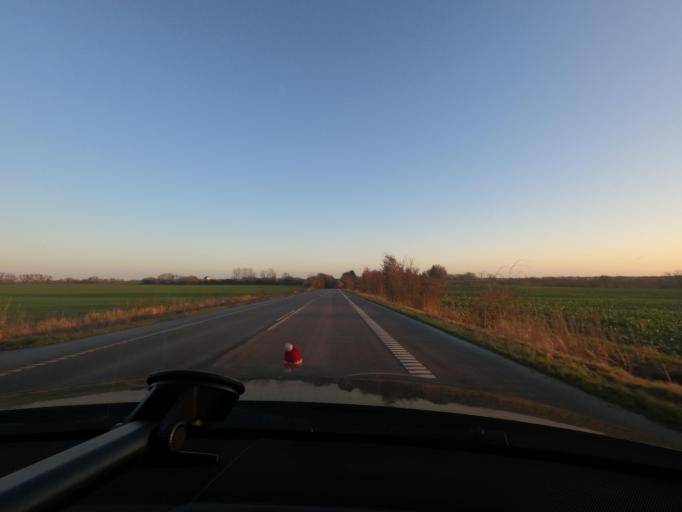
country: DK
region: South Denmark
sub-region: Sonderborg Kommune
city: Horuphav
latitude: 54.9001
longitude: 9.9557
